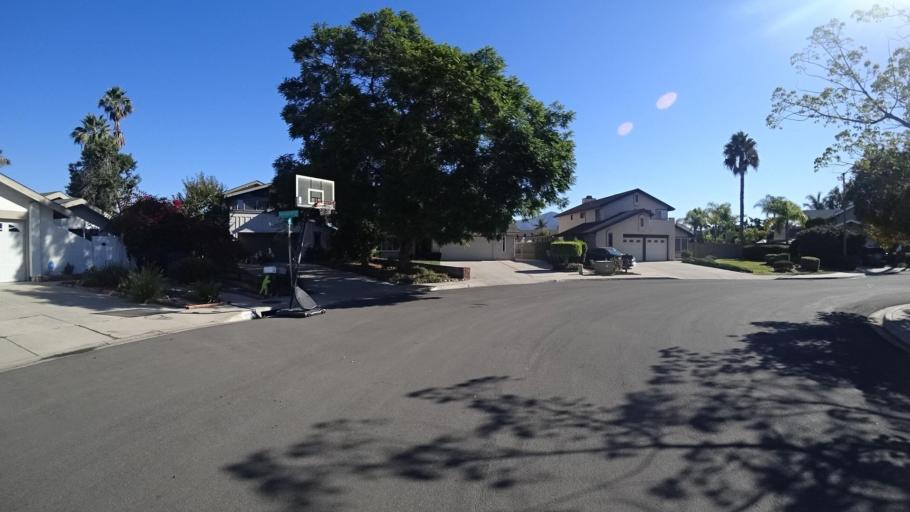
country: US
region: California
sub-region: San Diego County
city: Bonita
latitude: 32.6763
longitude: -117.0128
